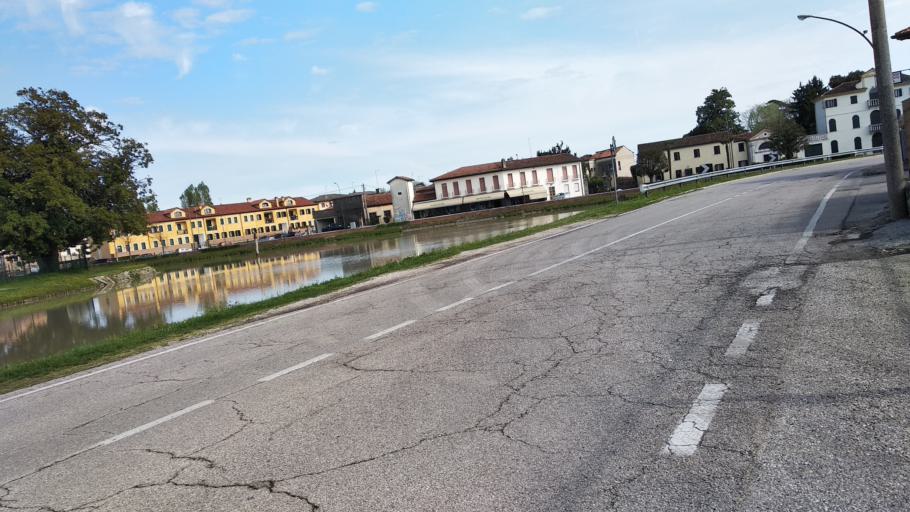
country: IT
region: Veneto
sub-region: Provincia di Venezia
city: Mira Taglio
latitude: 45.4358
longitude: 12.1374
